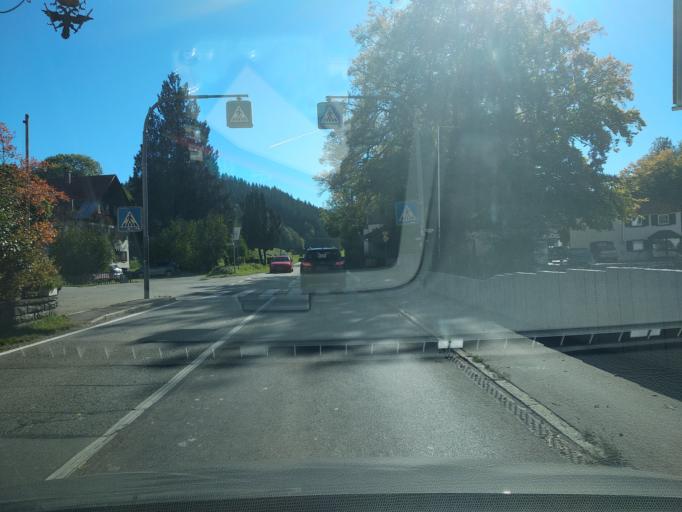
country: DE
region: Bavaria
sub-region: Swabia
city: Maierhofen
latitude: 47.6794
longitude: 10.0860
